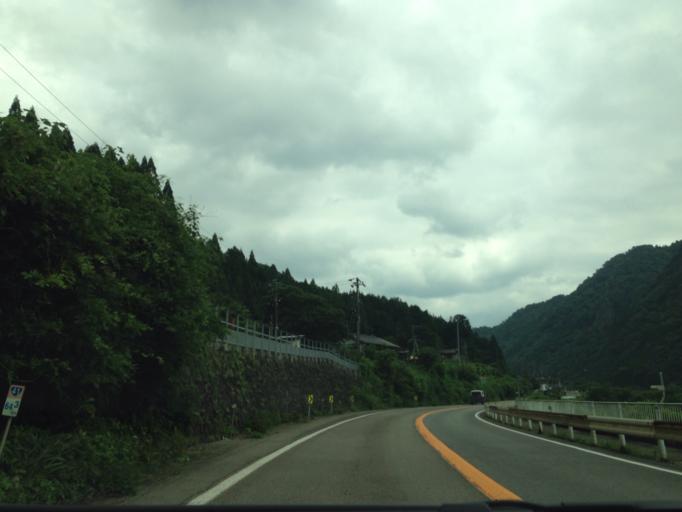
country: JP
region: Gifu
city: Mitake
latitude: 35.5848
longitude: 137.1725
